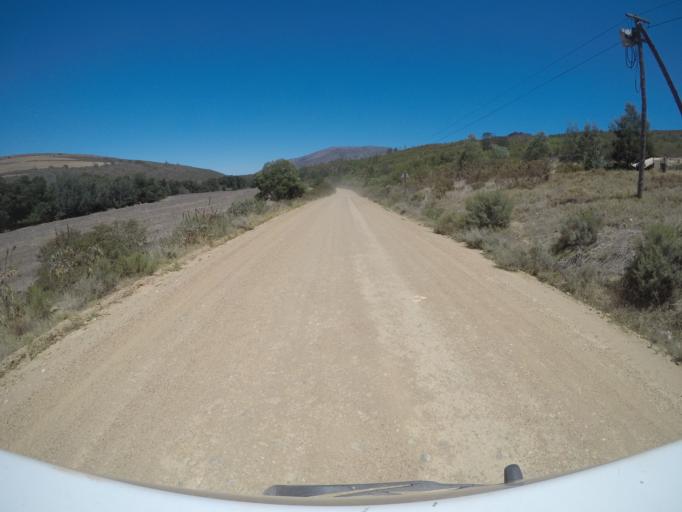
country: ZA
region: Western Cape
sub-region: Overberg District Municipality
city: Caledon
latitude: -34.1515
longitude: 19.2338
